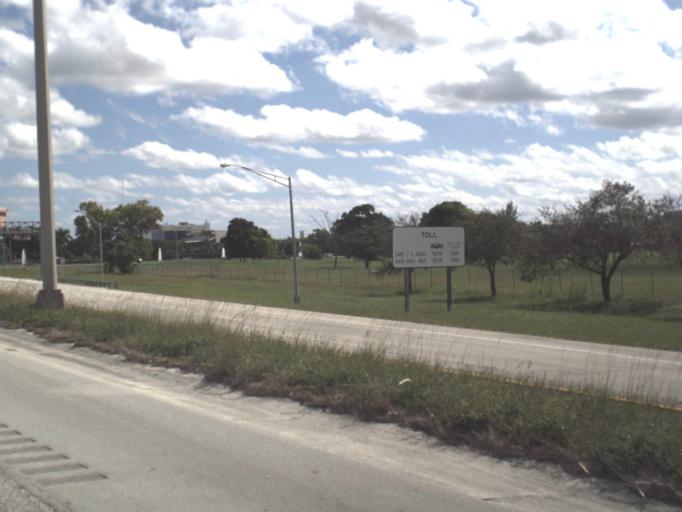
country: US
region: Florida
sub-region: Miami-Dade County
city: Lake Lucerne
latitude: 25.9721
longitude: -80.2503
